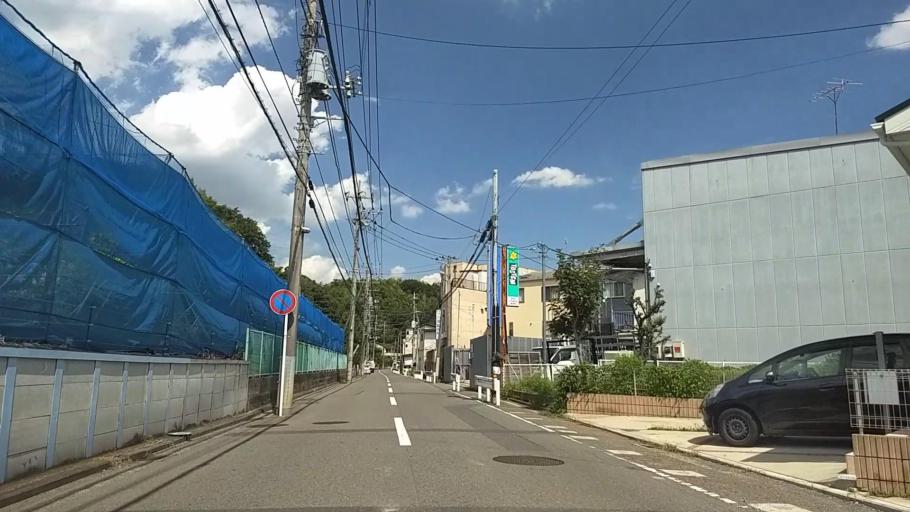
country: JP
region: Kanagawa
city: Yokohama
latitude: 35.5221
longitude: 139.5853
